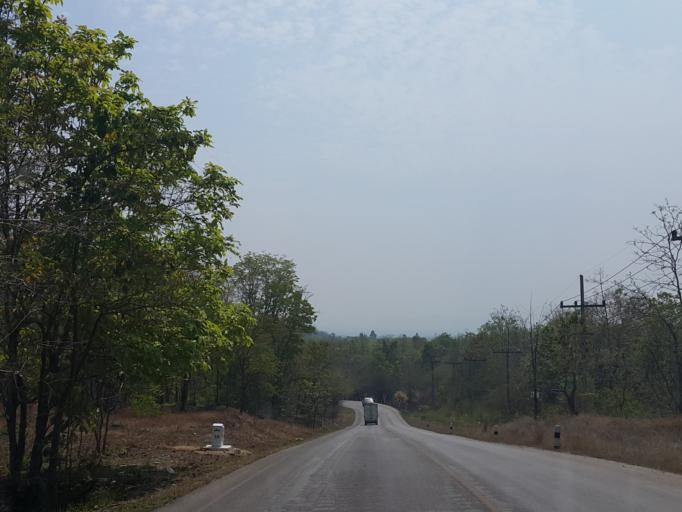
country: TH
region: Lampang
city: Mueang Pan
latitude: 18.7723
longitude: 99.5522
